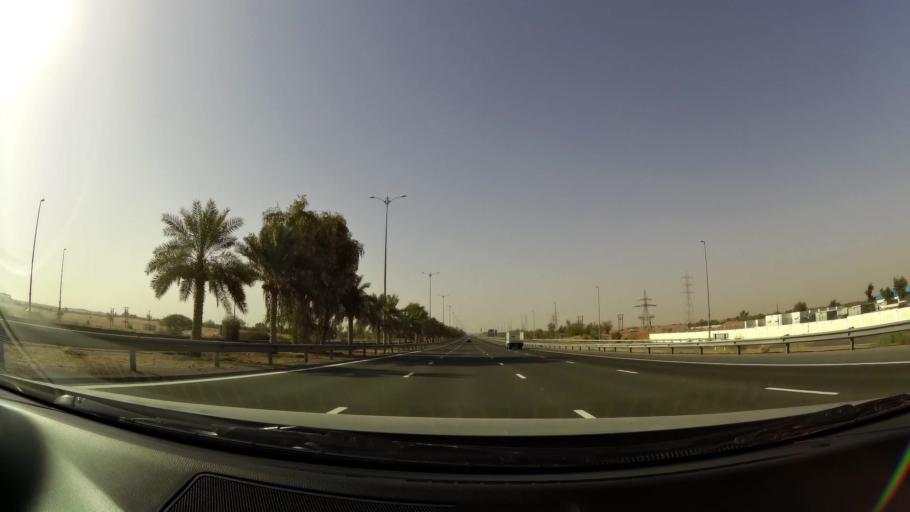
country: OM
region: Al Buraimi
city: Al Buraymi
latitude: 24.4833
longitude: 55.7737
